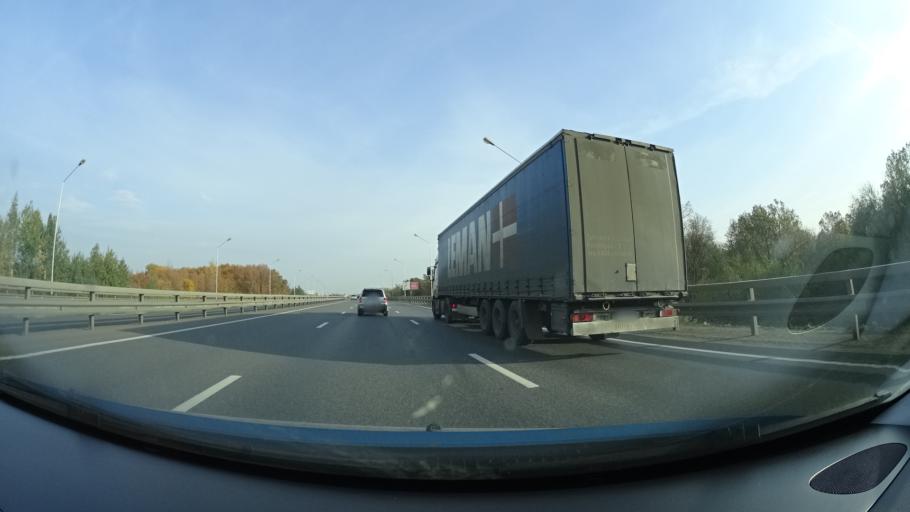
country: RU
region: Bashkortostan
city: Ufa
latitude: 54.6510
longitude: 55.9058
